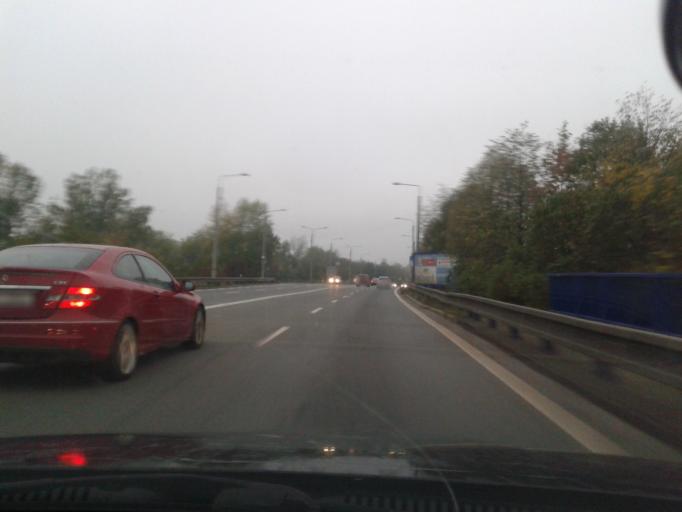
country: CZ
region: Moravskoslezsky
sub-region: Okres Ostrava-Mesto
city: Ostrava
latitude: 49.8039
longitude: 18.2962
